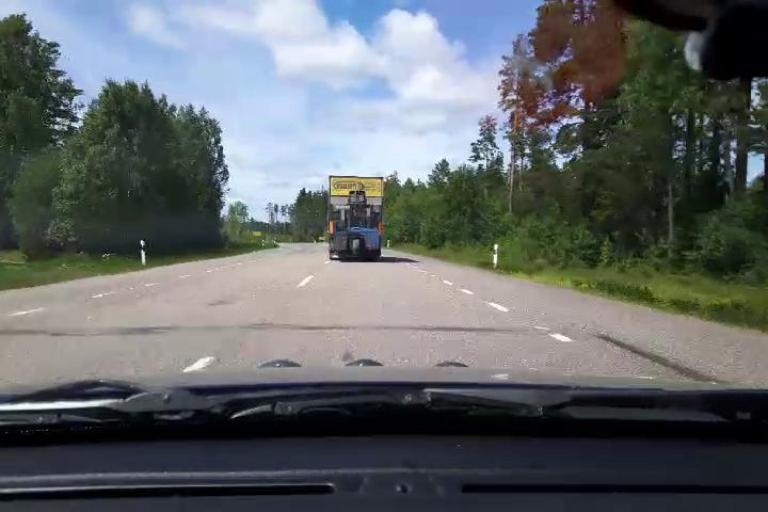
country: SE
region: Uppsala
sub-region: Osthammars Kommun
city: Bjorklinge
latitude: 60.1055
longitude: 17.5474
